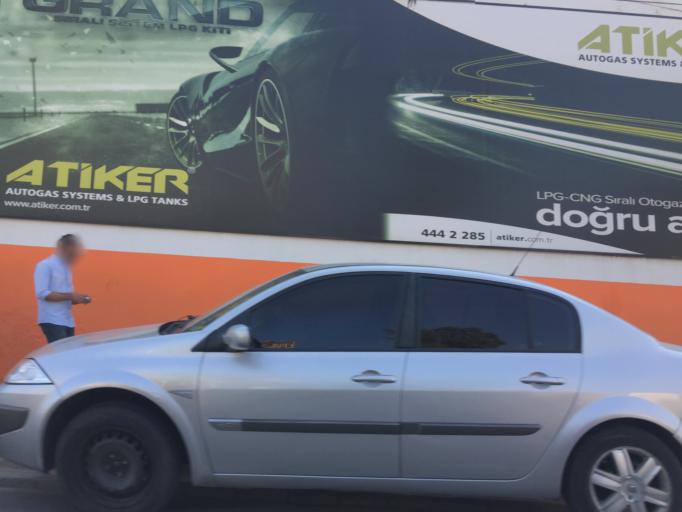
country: TR
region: Izmir
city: Buca
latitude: 38.4471
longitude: 27.1810
